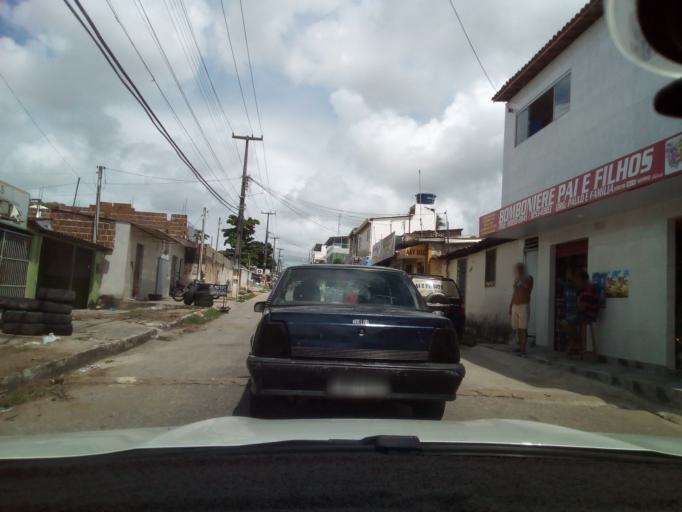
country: BR
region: Paraiba
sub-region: Bayeux
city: Bayeux
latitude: -7.1460
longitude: -34.9241
